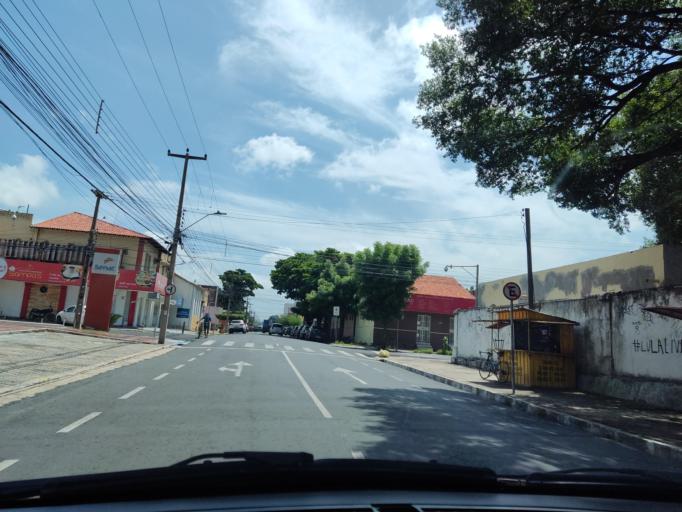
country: BR
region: Piaui
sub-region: Teresina
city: Teresina
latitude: -5.0853
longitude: -42.8178
